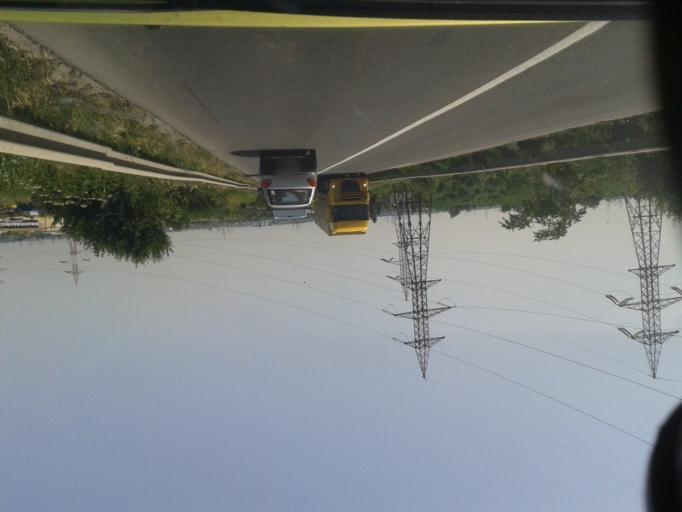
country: RO
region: Ilfov
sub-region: Comuna Glina
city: Catelu
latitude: 44.4217
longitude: 26.2364
